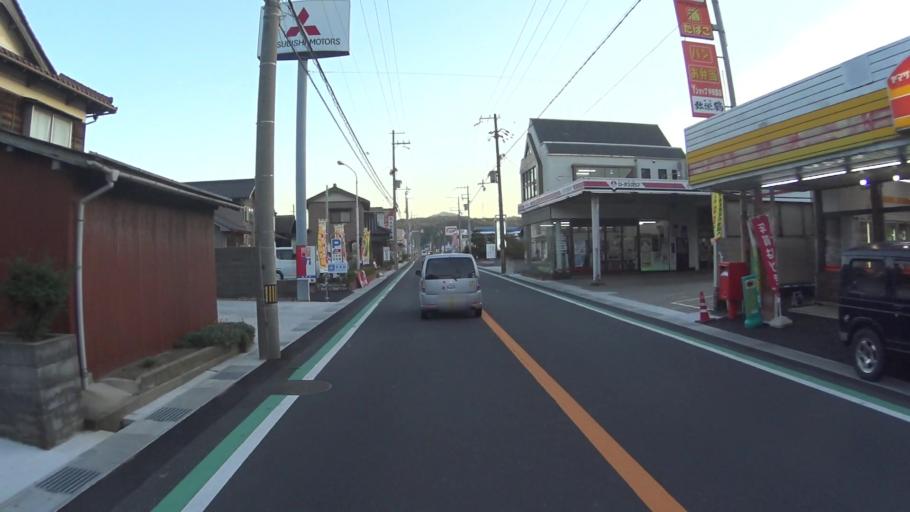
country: JP
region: Kyoto
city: Miyazu
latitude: 35.6739
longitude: 135.0280
